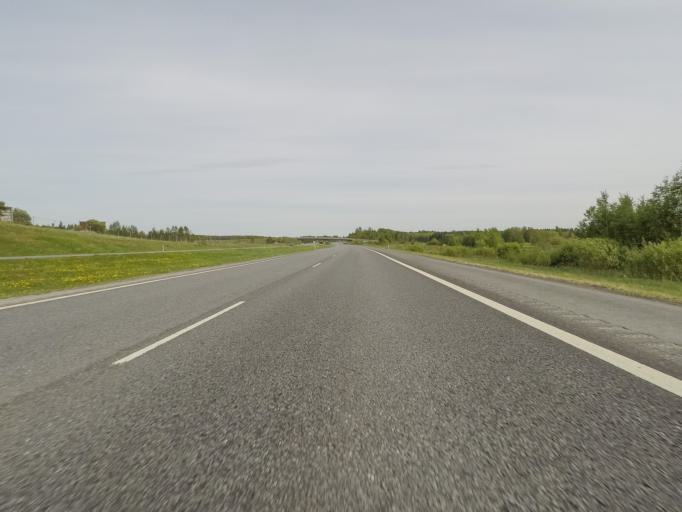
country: FI
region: Pirkanmaa
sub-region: Etelae-Pirkanmaa
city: Akaa
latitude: 61.1669
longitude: 23.9445
